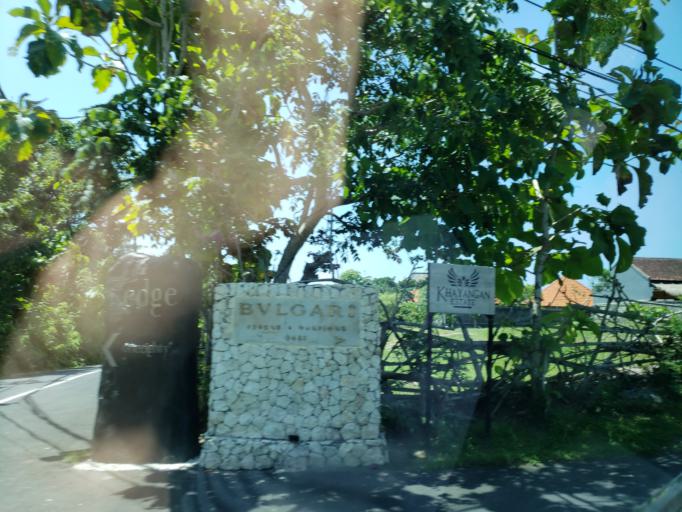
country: ID
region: Bali
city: Pecatu
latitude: -8.8414
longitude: 115.1228
